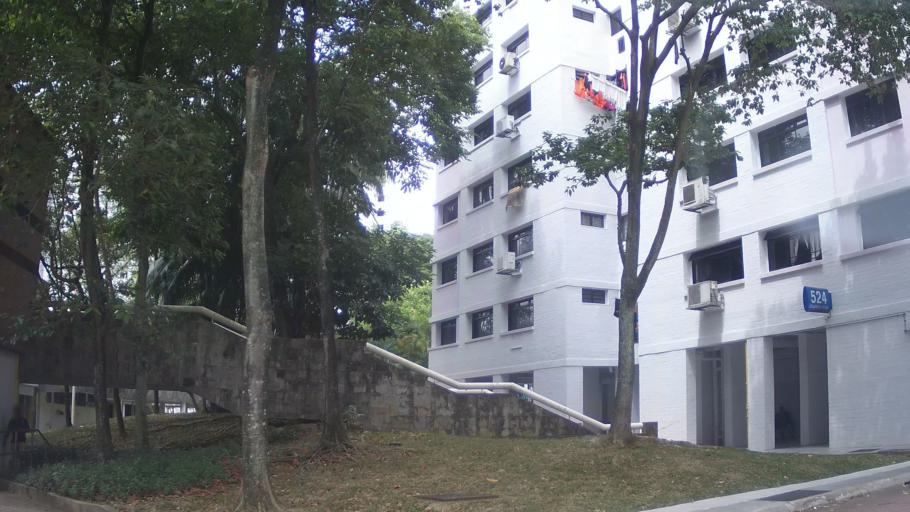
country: MY
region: Johor
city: Johor Bahru
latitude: 1.3860
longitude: 103.7664
